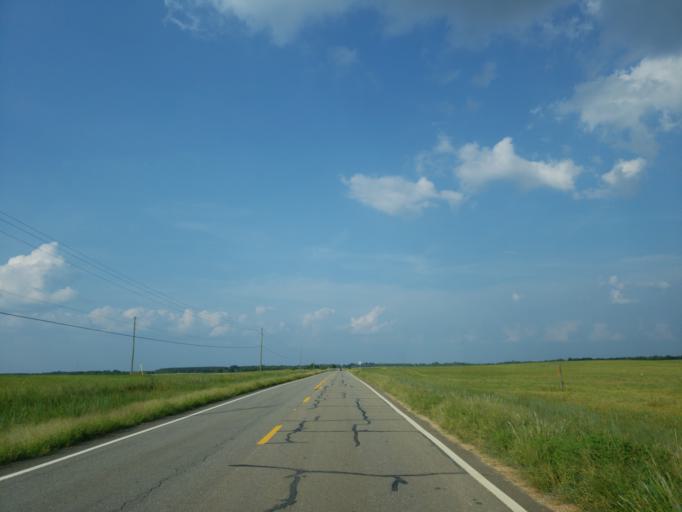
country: US
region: Alabama
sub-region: Greene County
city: Eutaw
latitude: 32.8050
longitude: -87.9549
